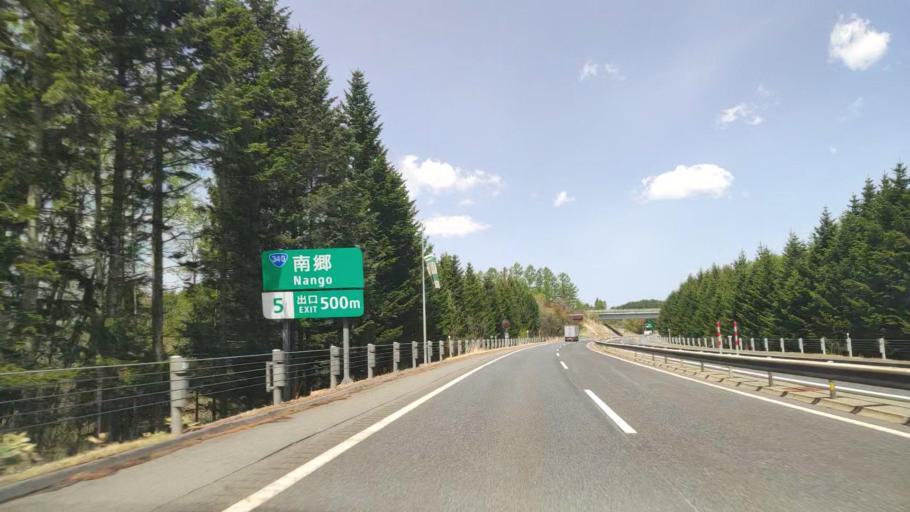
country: JP
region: Aomori
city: Hachinohe
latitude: 40.4002
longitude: 141.4451
